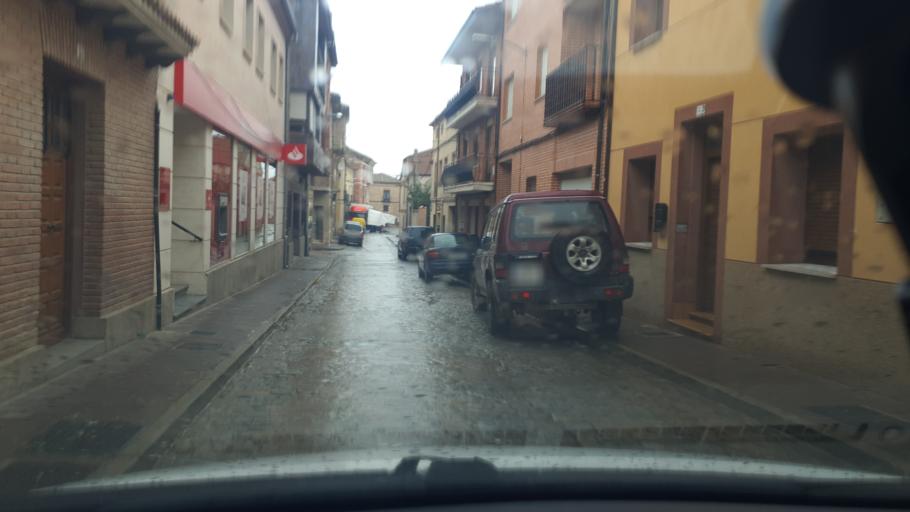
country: ES
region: Castille and Leon
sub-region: Provincia de Segovia
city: Carbonero el Mayor
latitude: 41.1214
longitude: -4.2651
